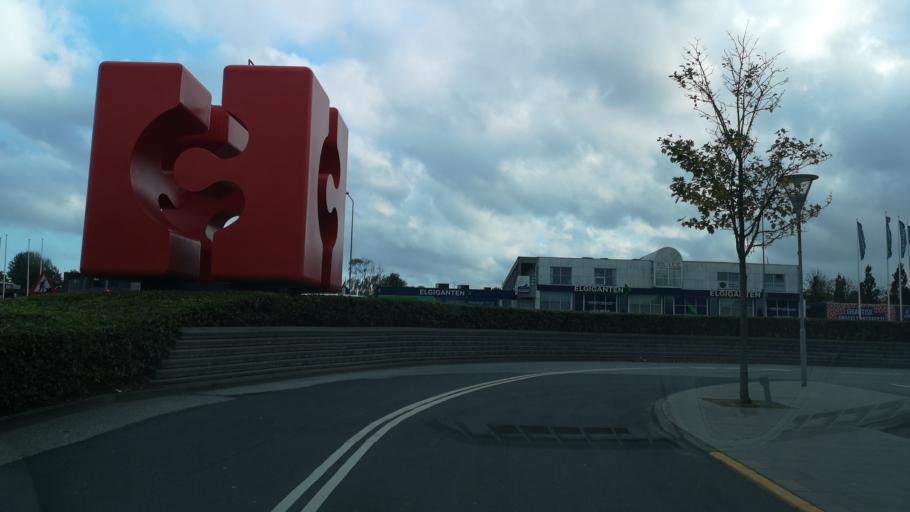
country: DK
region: Central Jutland
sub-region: Herning Kommune
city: Herning
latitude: 56.1352
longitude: 8.9989
